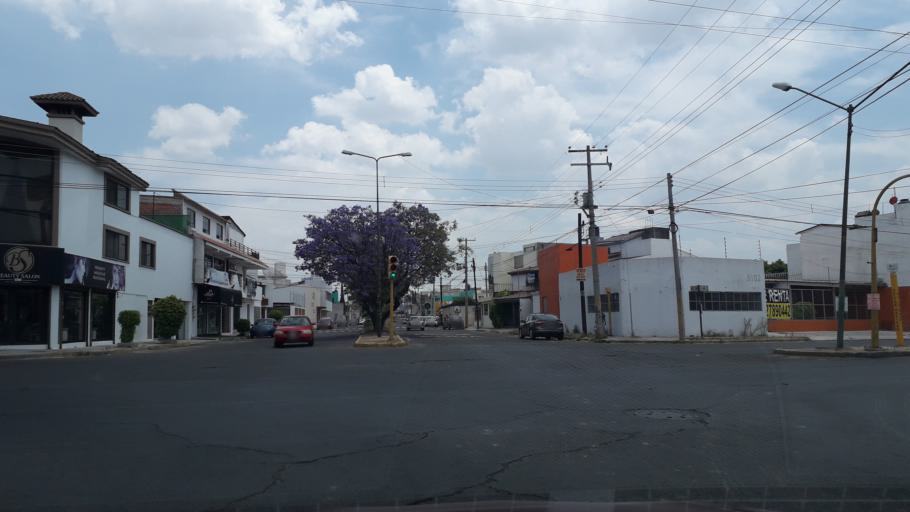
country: MX
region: Puebla
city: Puebla
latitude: 19.0176
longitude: -98.1955
